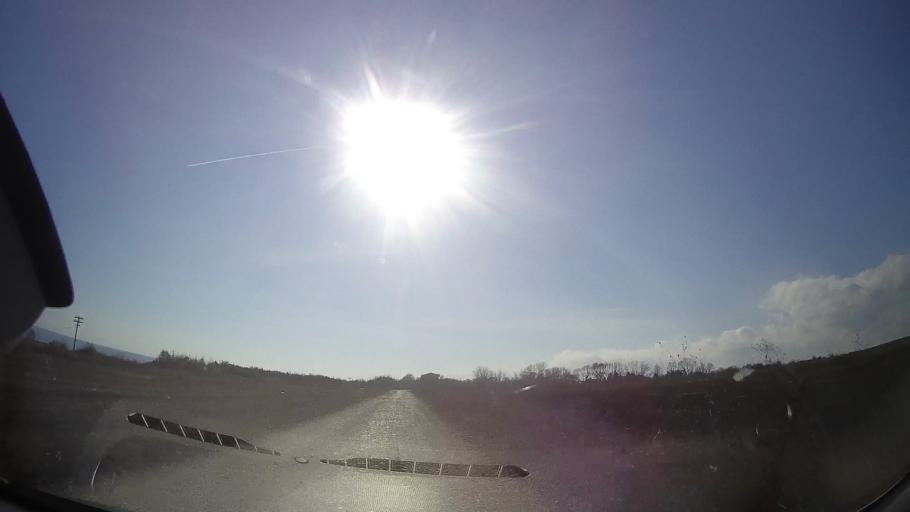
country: RO
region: Constanta
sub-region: Comuna Douazeci si Trei August
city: Douazeci si Trei August
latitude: 43.9059
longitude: 28.6189
